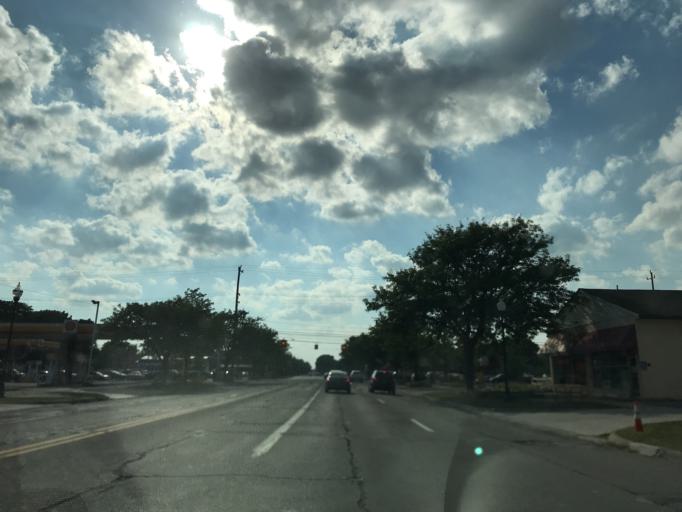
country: US
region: Michigan
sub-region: Wayne County
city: Redford
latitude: 42.3996
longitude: -83.2944
